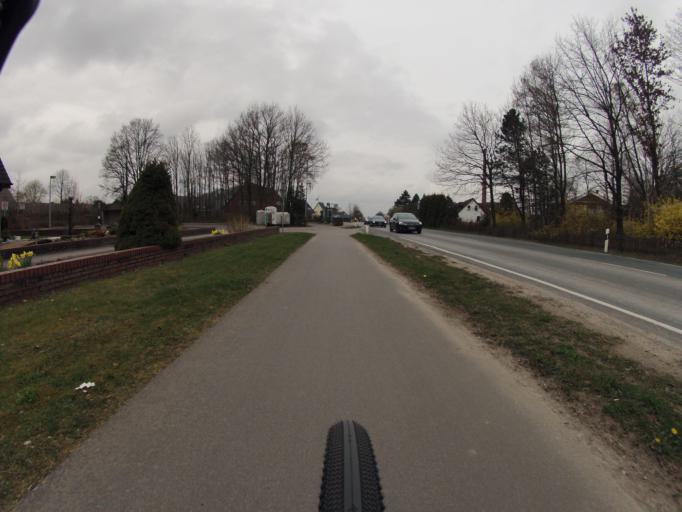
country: DE
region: North Rhine-Westphalia
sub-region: Regierungsbezirk Munster
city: Mettingen
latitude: 52.3377
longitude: 7.7408
